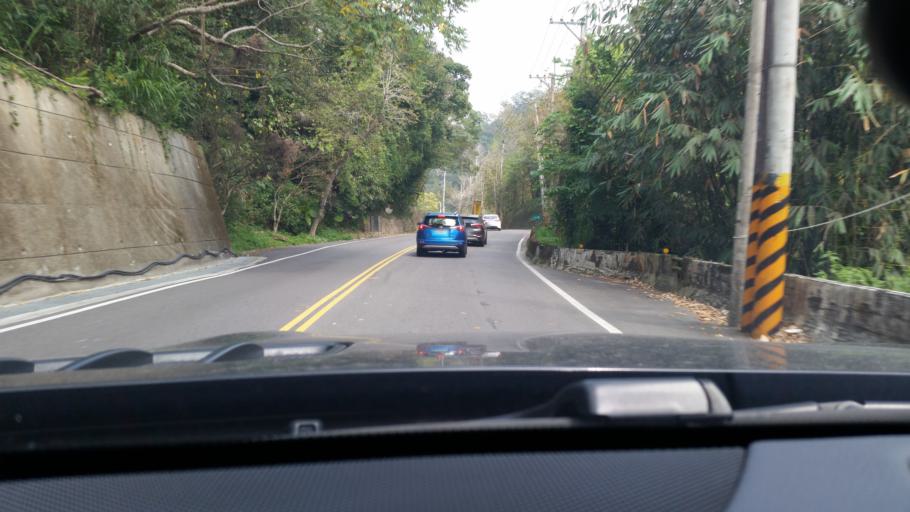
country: TW
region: Taiwan
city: Daxi
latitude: 24.8294
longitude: 121.3171
